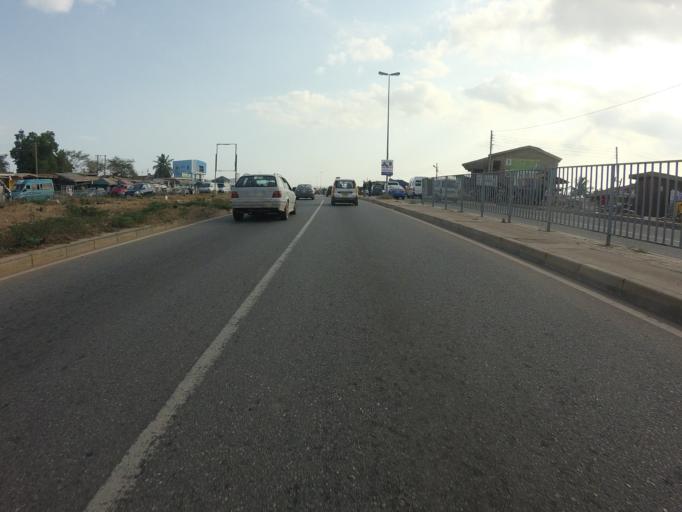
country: GH
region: Greater Accra
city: Achiaman
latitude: 5.6461
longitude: -0.3099
